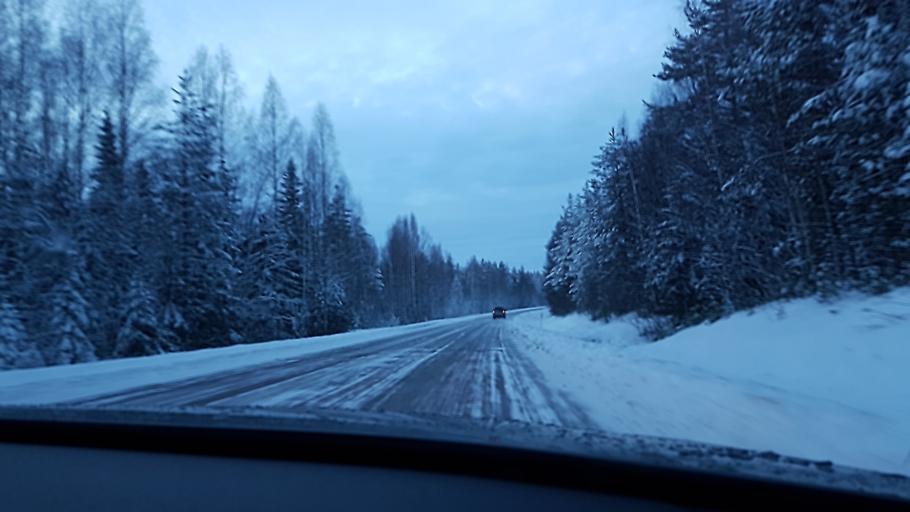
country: SE
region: Jaemtland
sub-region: Harjedalens Kommun
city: Sveg
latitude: 62.0450
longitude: 14.8680
